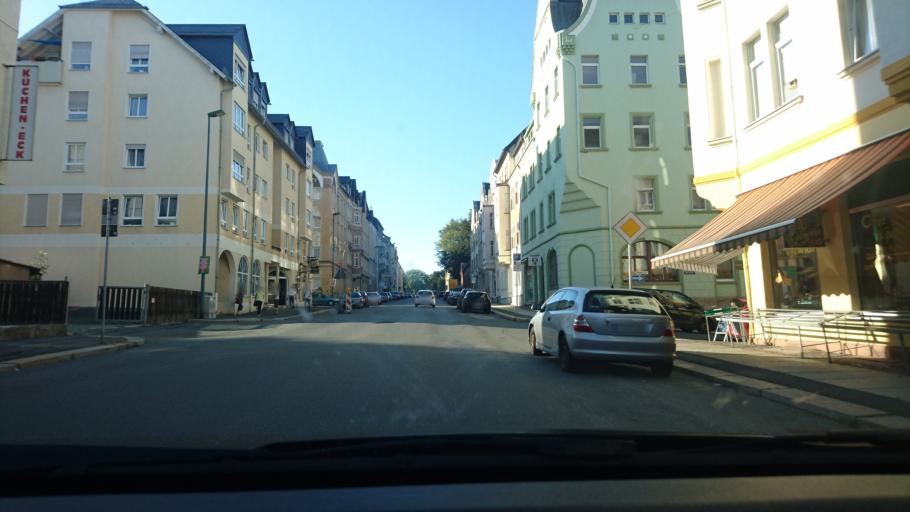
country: DE
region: Saxony
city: Auerbach
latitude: 50.5072
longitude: 12.3939
